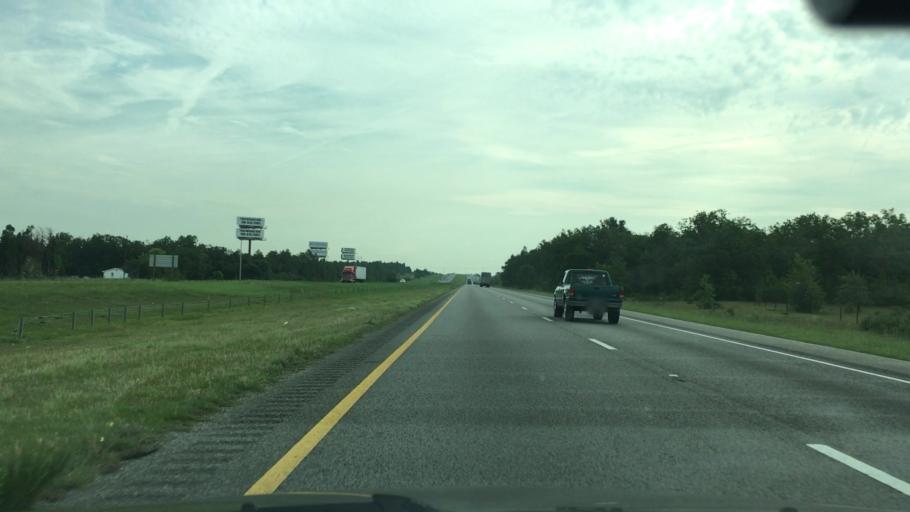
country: US
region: South Carolina
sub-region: Lexington County
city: Batesburg
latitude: 33.7123
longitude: -81.5807
